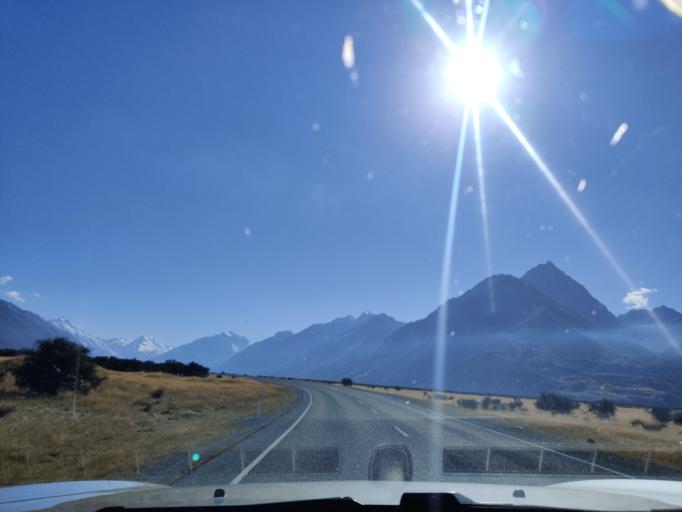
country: NZ
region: Canterbury
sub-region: Timaru District
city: Pleasant Point
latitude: -43.7837
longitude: 170.1225
